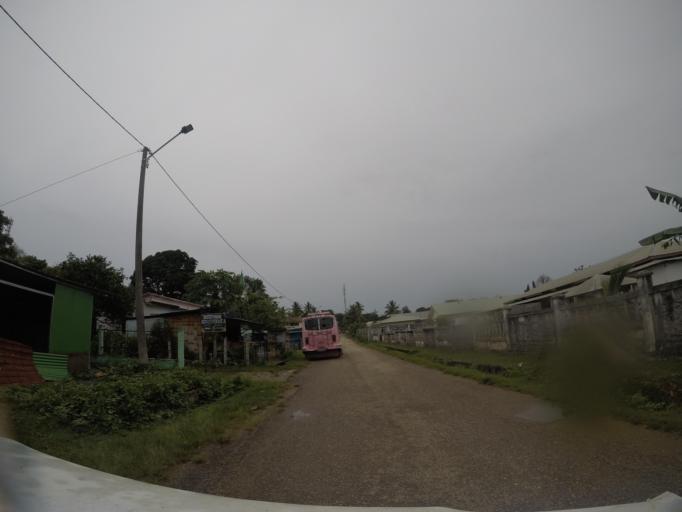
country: TL
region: Lautem
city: Lospalos
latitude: -8.5224
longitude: 126.9986
